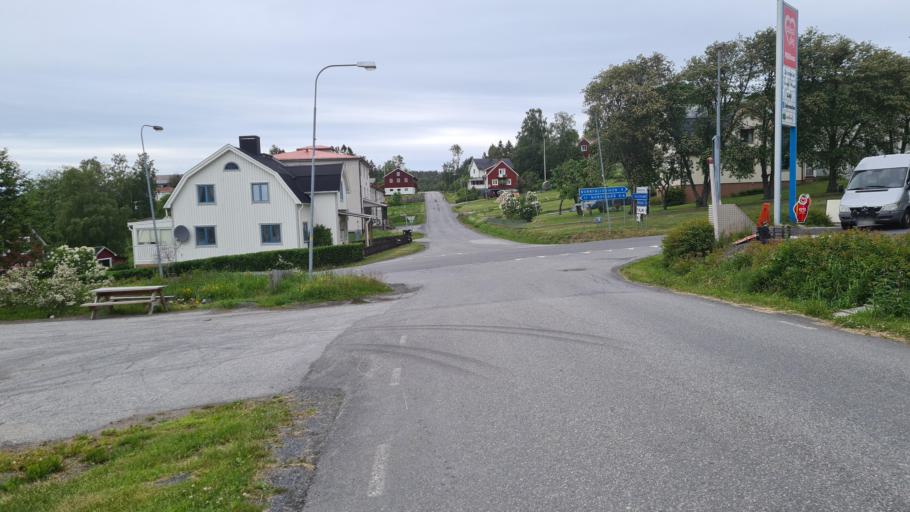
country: SE
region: Vaesternorrland
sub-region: Kramfors Kommun
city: Nordingra
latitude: 62.9856
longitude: 18.4317
